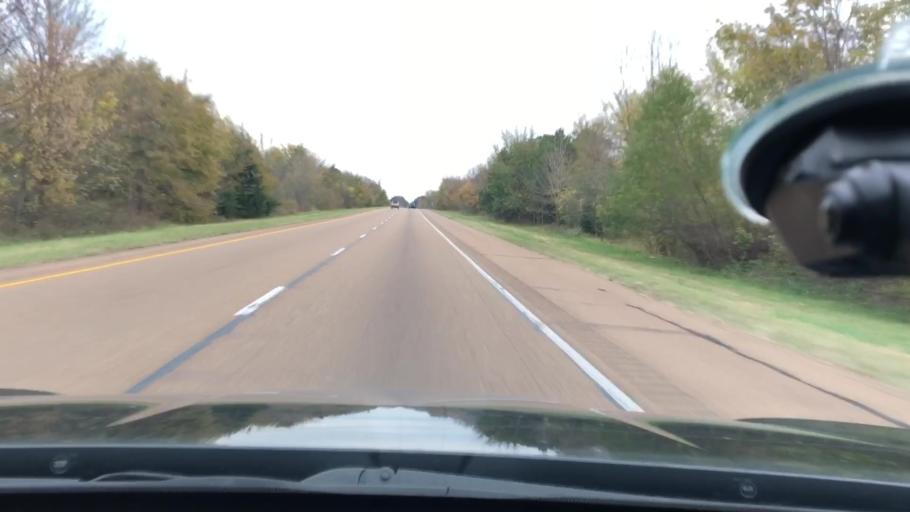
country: US
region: Arkansas
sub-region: Hempstead County
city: Hope
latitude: 33.7523
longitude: -93.5029
